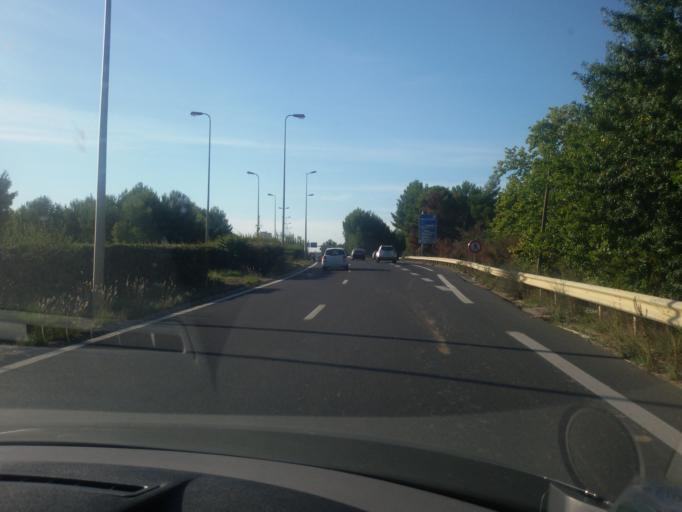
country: FR
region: Languedoc-Roussillon
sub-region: Departement de l'Herault
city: Lattes
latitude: 43.5856
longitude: 3.8958
